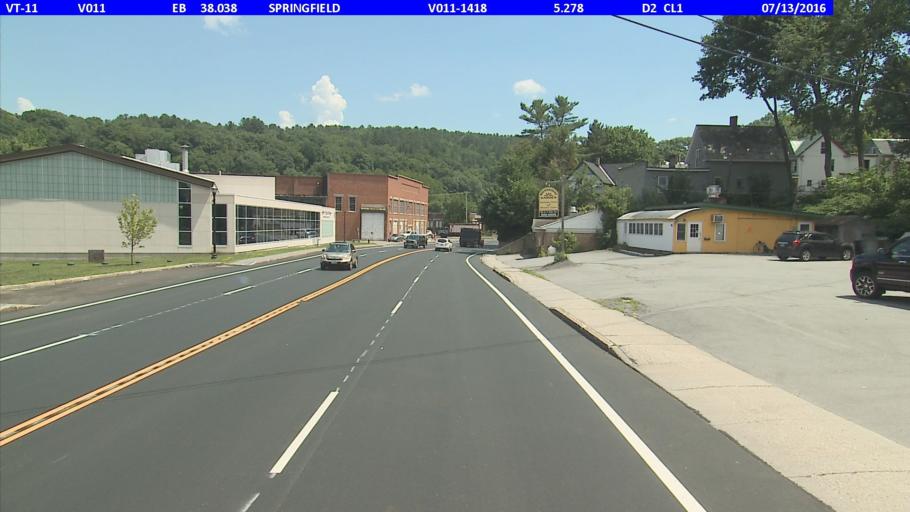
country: US
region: Vermont
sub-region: Windsor County
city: Springfield
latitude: 43.2917
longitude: -72.4744
